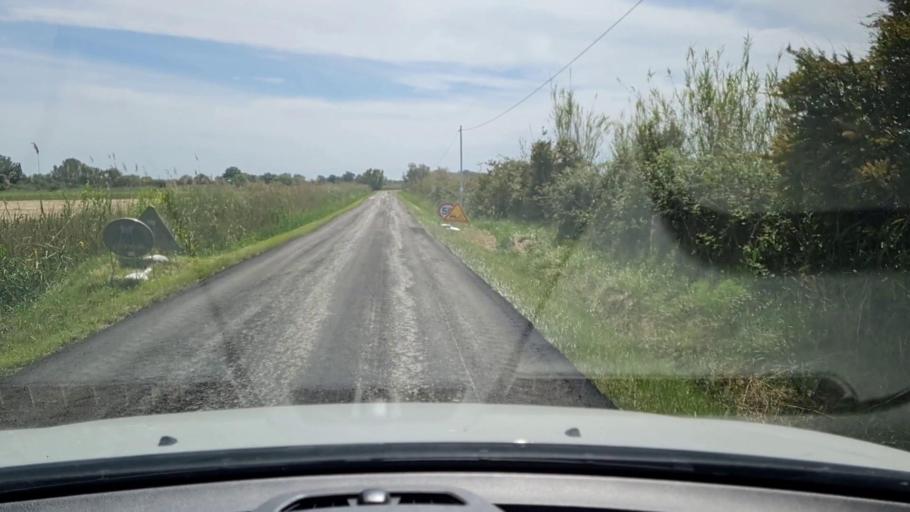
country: FR
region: Provence-Alpes-Cote d'Azur
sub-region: Departement des Bouches-du-Rhone
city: Saintes-Maries-de-la-Mer
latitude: 43.5578
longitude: 4.3811
